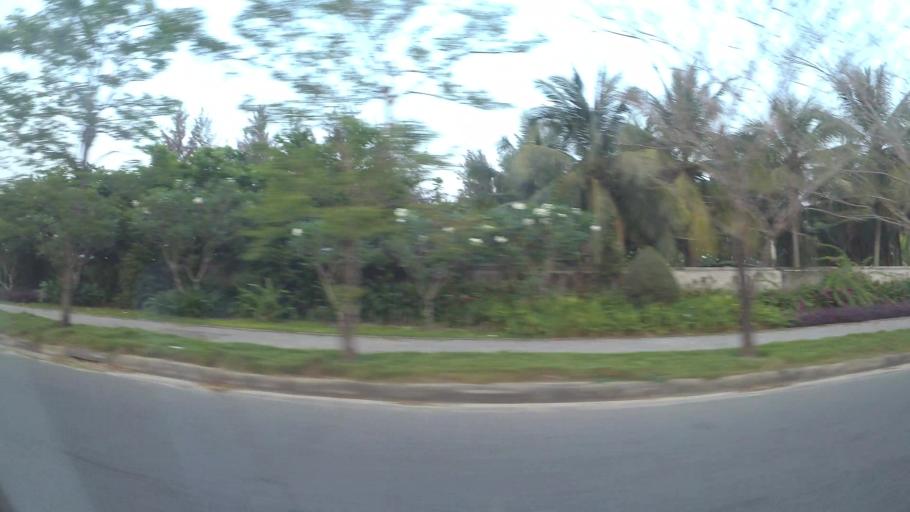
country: VN
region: Da Nang
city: Ngu Hanh Son
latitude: 16.0201
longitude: 108.2587
